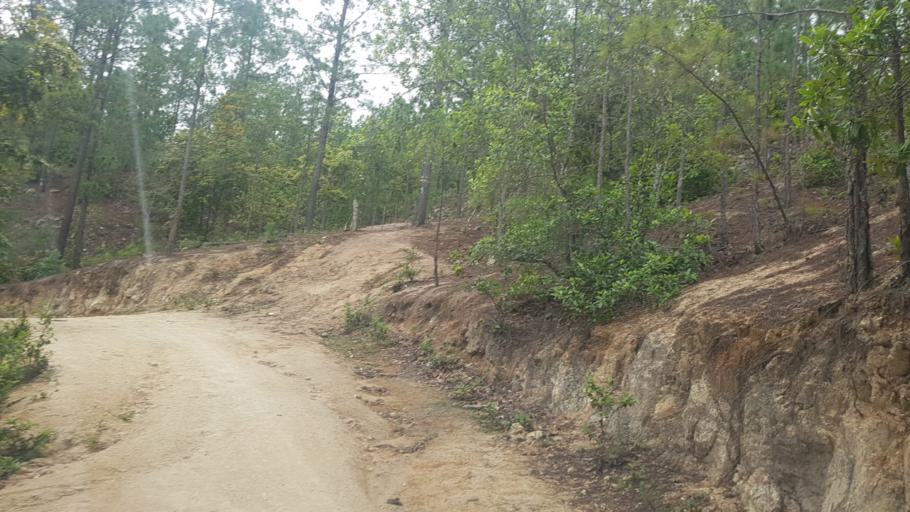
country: NI
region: Madriz
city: Totogalpa
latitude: 13.6140
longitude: -86.6104
